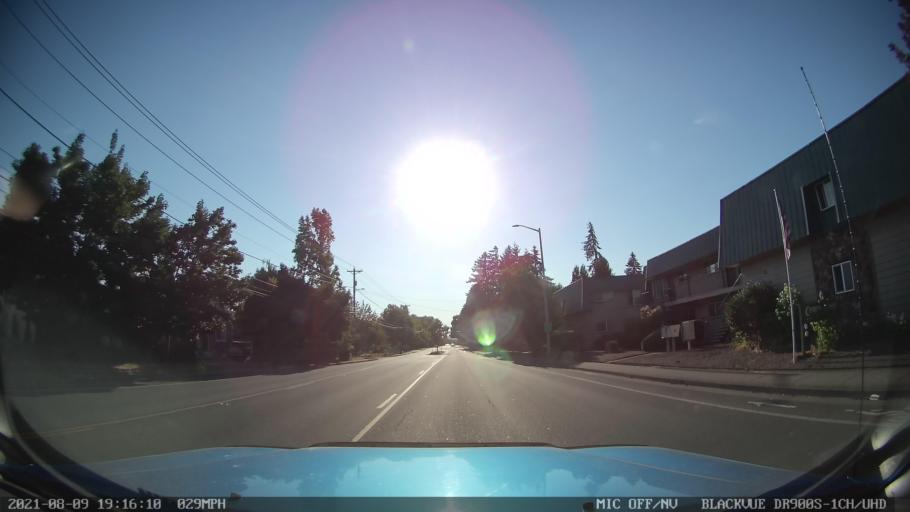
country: US
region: Oregon
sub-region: Marion County
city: Four Corners
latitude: 44.9399
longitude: -122.9936
